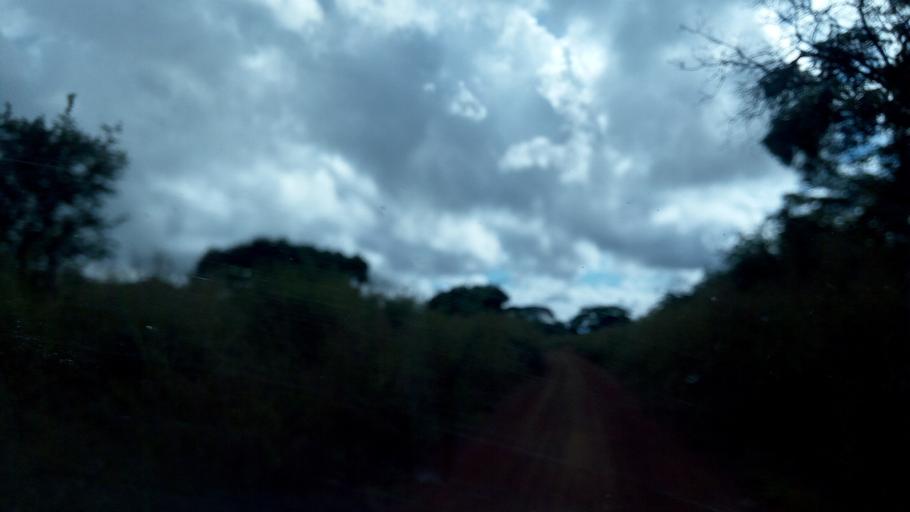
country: ZM
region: Northern
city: Kaputa
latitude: -8.3775
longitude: 28.9589
